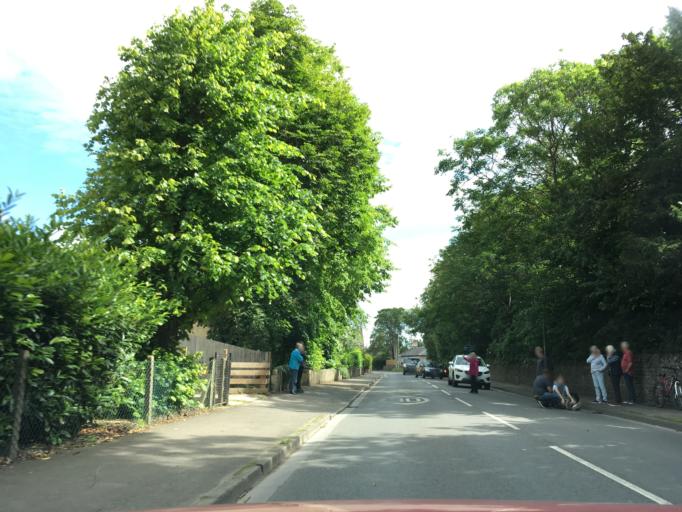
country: GB
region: England
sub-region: Gloucestershire
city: Lechlade
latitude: 51.6985
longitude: -1.6903
